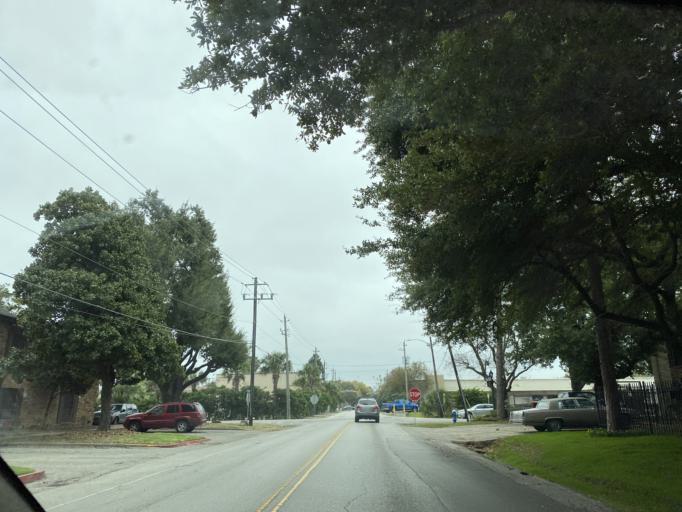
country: US
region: Texas
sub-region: Harris County
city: Hunters Creek Village
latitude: 29.7335
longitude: -95.4898
